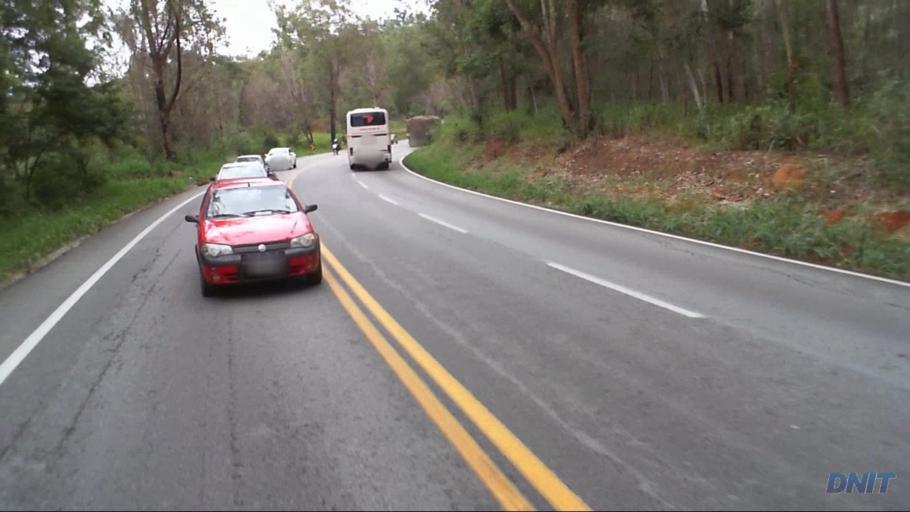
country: BR
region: Minas Gerais
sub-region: Joao Monlevade
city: Joao Monlevade
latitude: -19.8548
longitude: -43.1116
